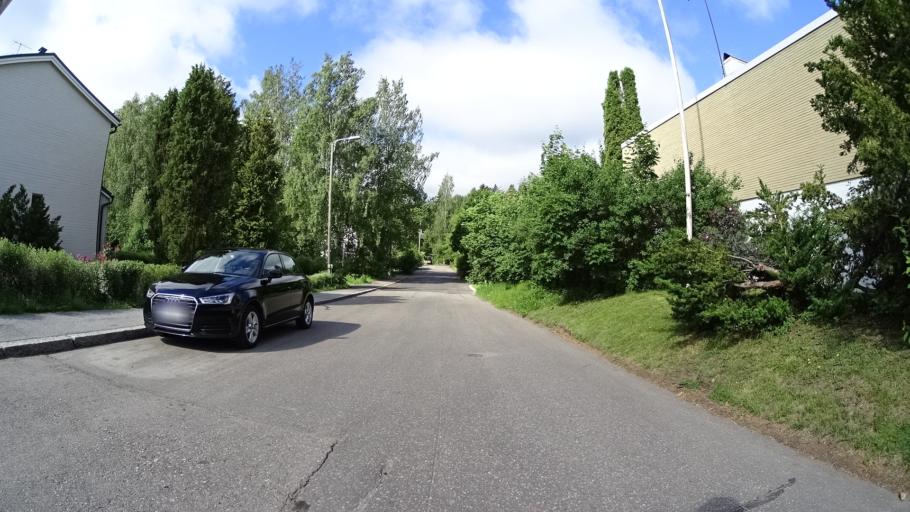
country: FI
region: Uusimaa
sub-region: Helsinki
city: Teekkarikylae
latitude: 60.2286
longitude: 24.8418
